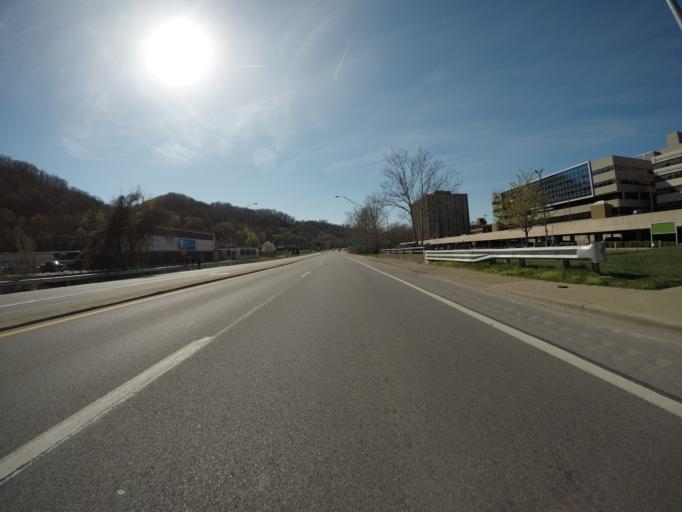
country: US
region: West Virginia
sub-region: Kanawha County
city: Charleston
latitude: 38.3286
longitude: -81.6015
